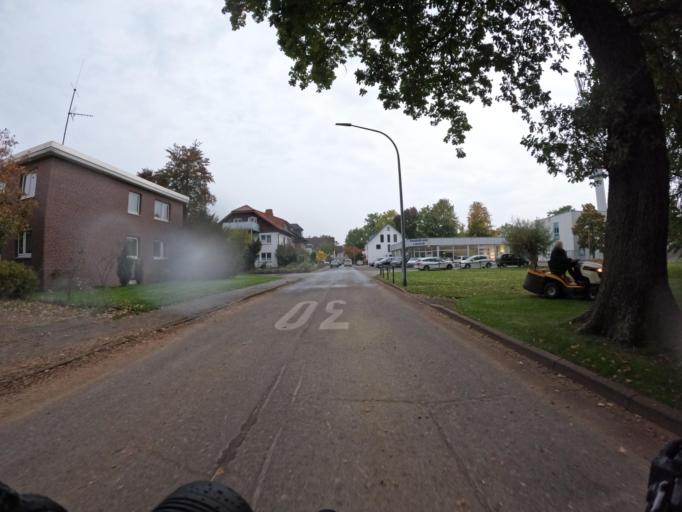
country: DE
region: North Rhine-Westphalia
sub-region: Regierungsbezirk Detmold
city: Hovelhof
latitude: 51.8203
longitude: 8.6622
